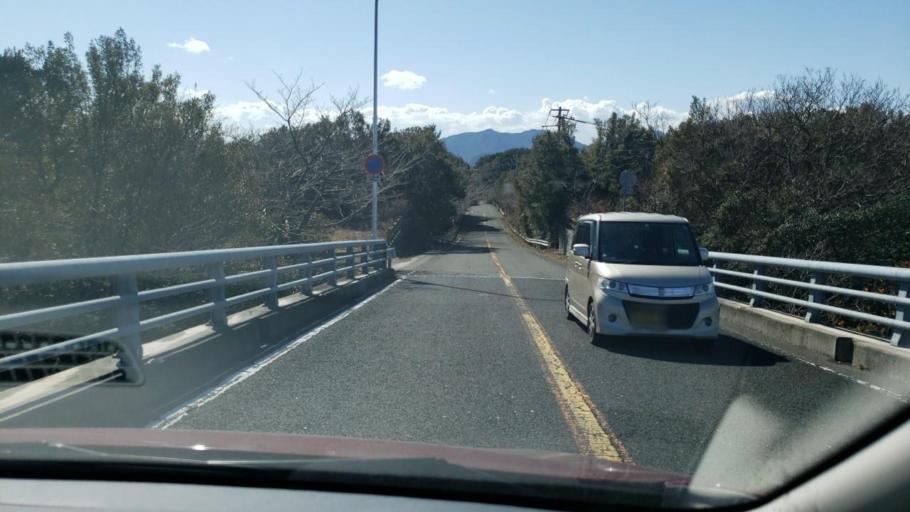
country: JP
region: Tokushima
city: Narutocho-mitsuishi
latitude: 34.2313
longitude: 134.6018
